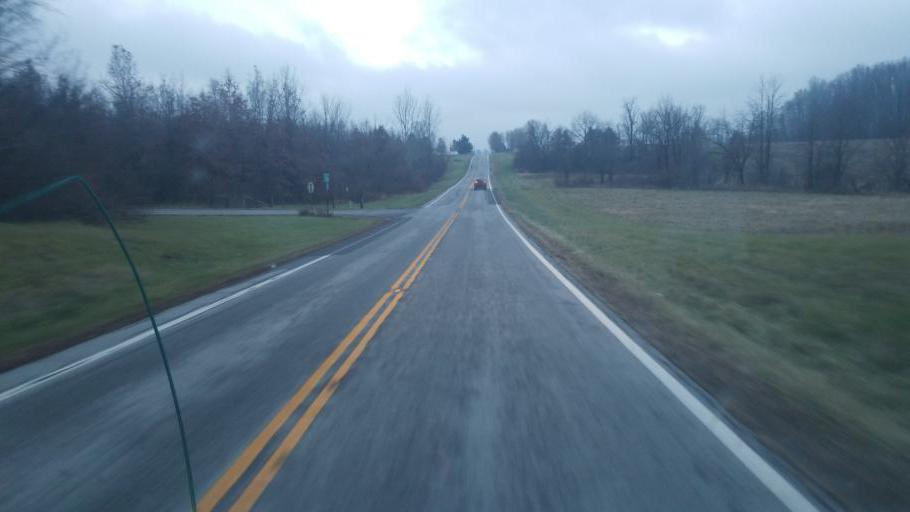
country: US
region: Ohio
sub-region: Wyandot County
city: Upper Sandusky
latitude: 40.9171
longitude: -83.1312
